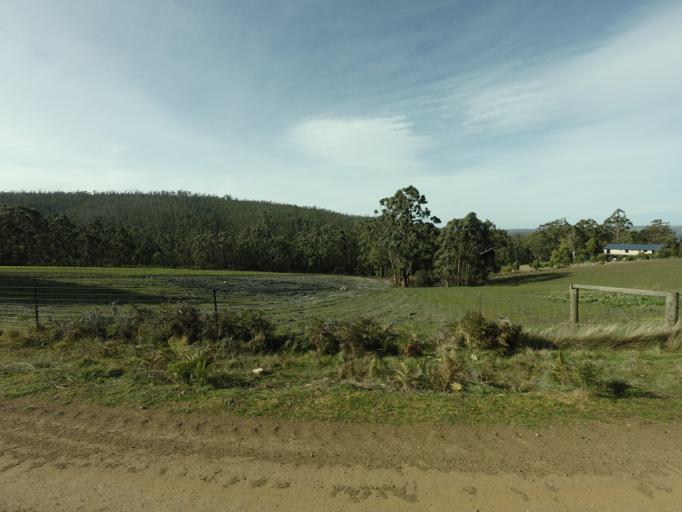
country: AU
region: Tasmania
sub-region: Kingborough
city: Kettering
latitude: -43.0985
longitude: 147.2632
